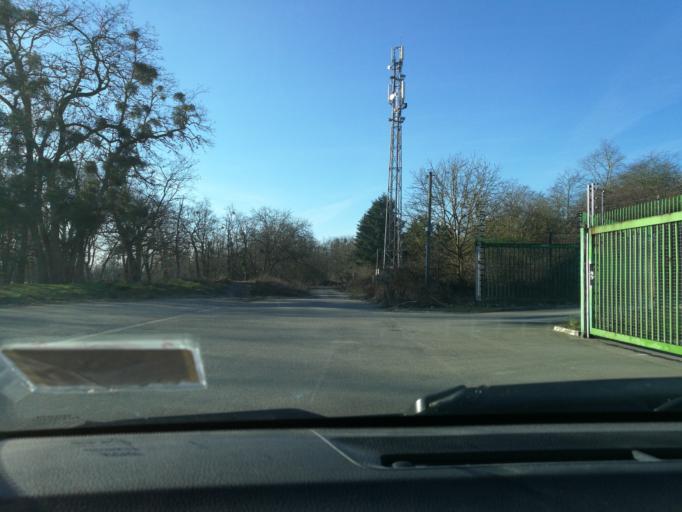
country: FR
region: Centre
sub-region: Departement du Loiret
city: Ingre
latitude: 47.9107
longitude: 1.8214
